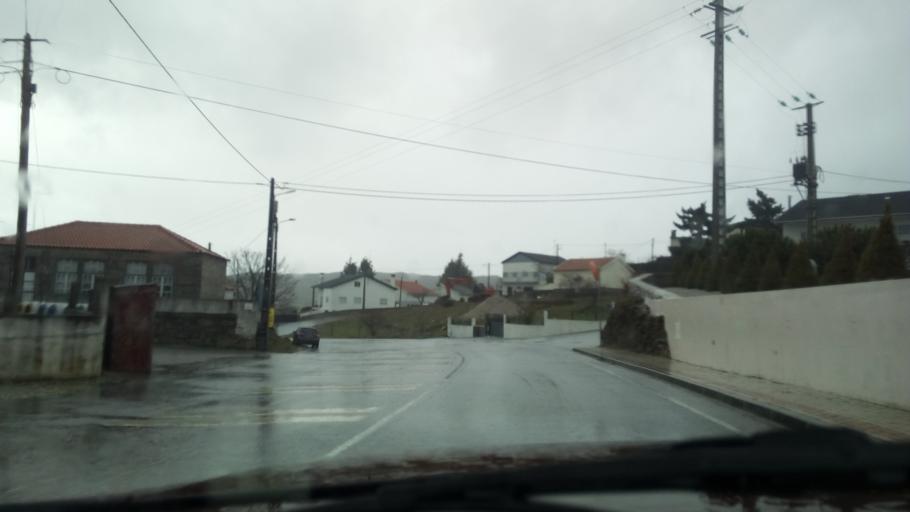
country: PT
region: Guarda
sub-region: Guarda
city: Guarda
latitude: 40.5414
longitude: -7.2953
